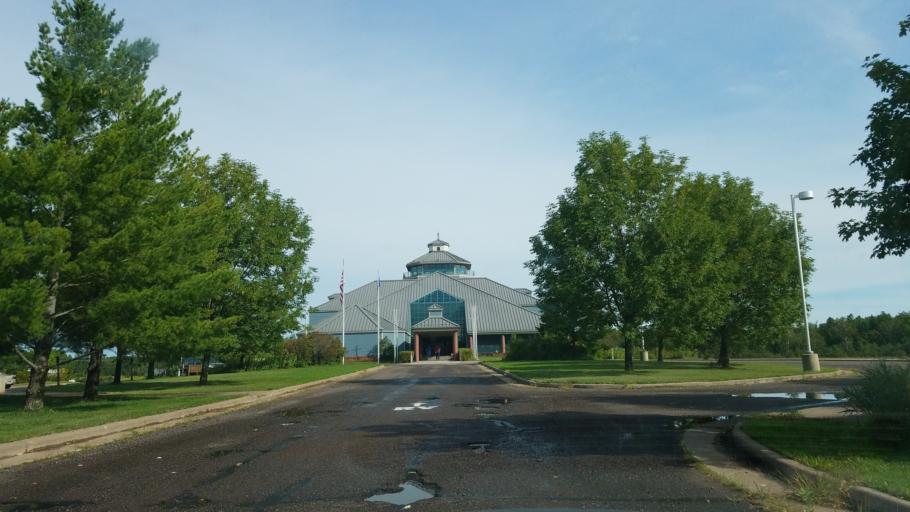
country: US
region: Wisconsin
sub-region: Ashland County
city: Ashland
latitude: 46.5836
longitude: -90.9639
